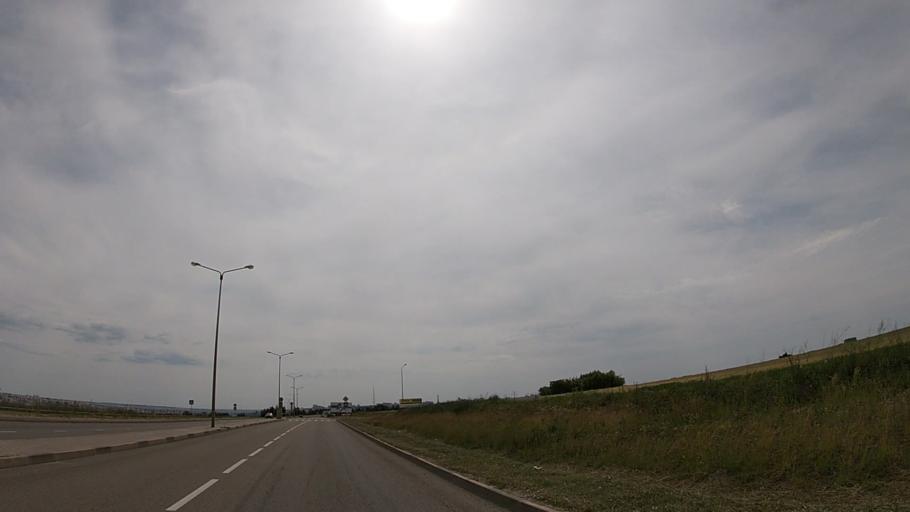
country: RU
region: Belgorod
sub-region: Belgorodskiy Rayon
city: Belgorod
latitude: 50.5944
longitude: 36.5255
